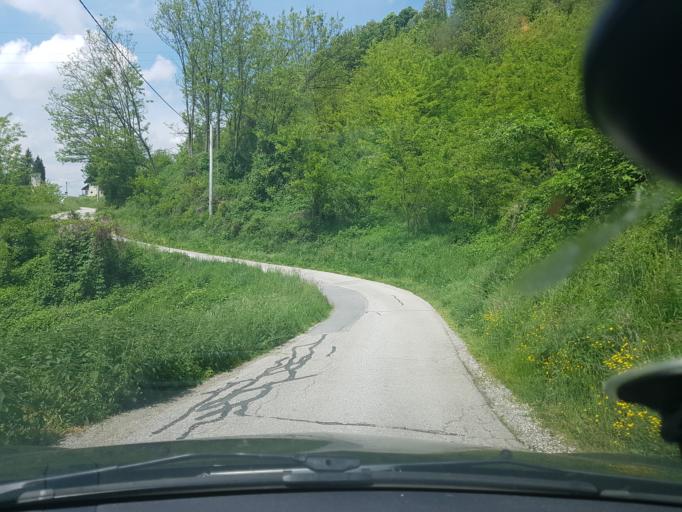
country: SI
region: Rogatec
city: Rogatec
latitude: 46.2137
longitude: 15.7164
